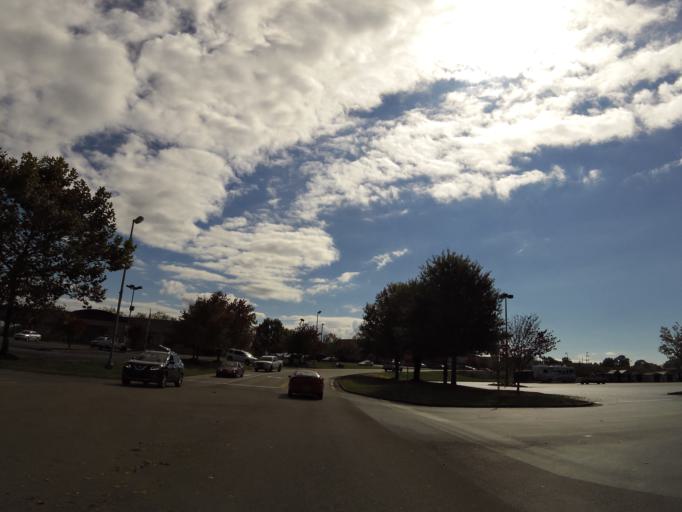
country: US
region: Tennessee
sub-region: Blount County
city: Maryville
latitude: 35.7680
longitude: -83.9888
